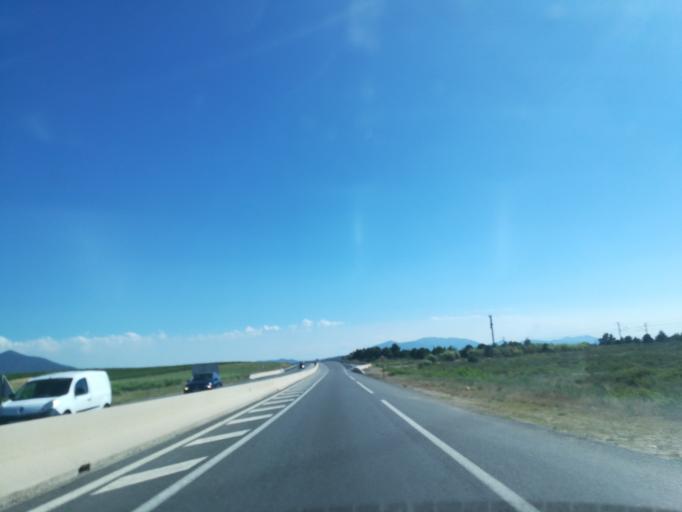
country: FR
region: Languedoc-Roussillon
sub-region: Departement des Pyrenees-Orientales
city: Villemolaque
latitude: 42.5883
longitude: 2.8514
